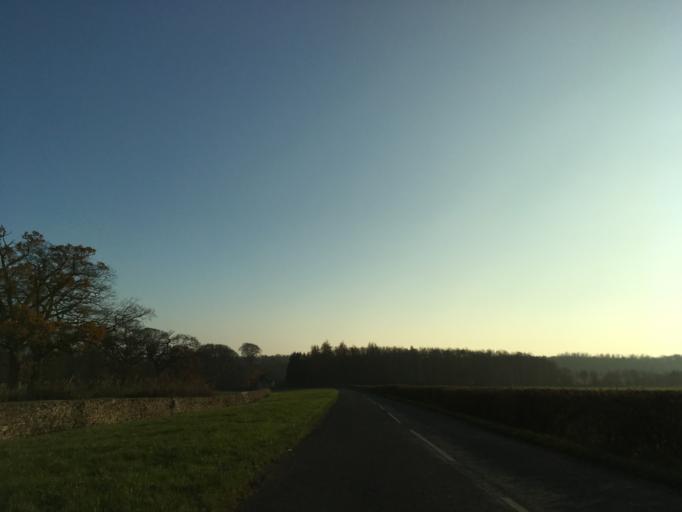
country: GB
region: England
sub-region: Wiltshire
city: Luckington
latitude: 51.5490
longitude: -2.2933
